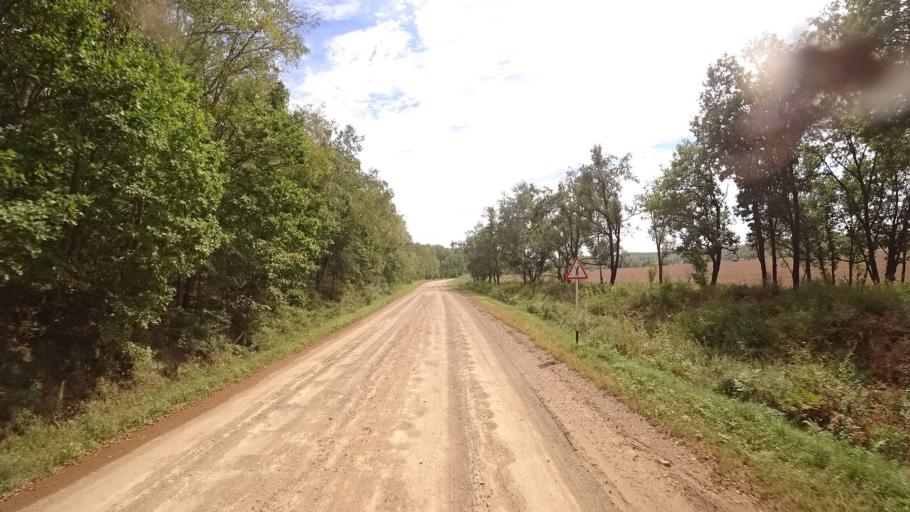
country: RU
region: Primorskiy
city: Yakovlevka
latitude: 44.5709
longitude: 133.5936
